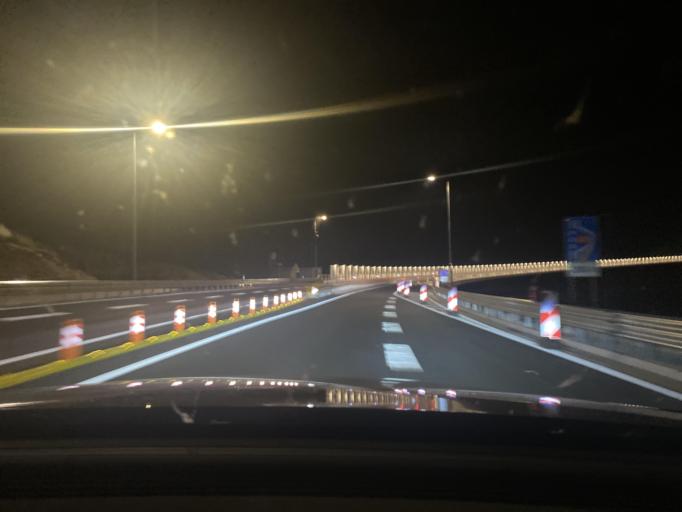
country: BA
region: Federation of Bosnia and Herzegovina
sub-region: Hercegovacko-Bosanski Kanton
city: Neum
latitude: 42.9420
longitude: 17.5433
